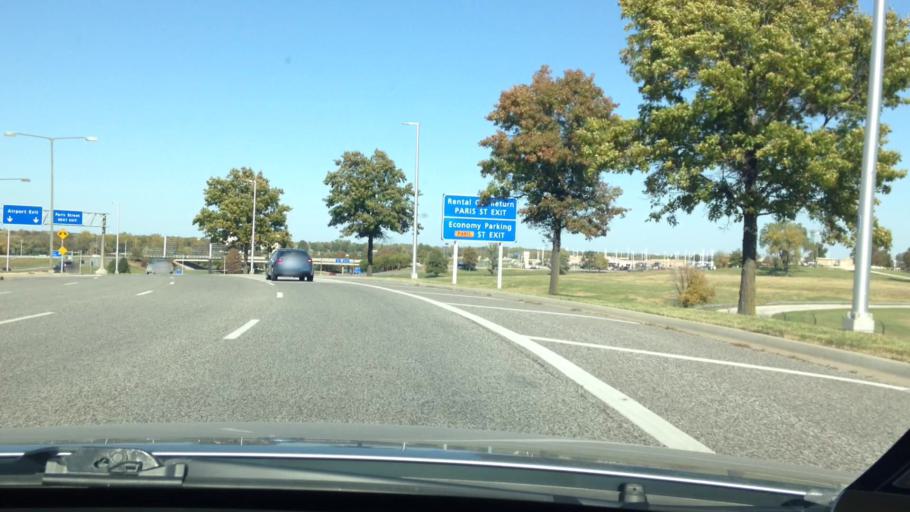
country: US
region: Missouri
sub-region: Platte County
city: Weatherby Lake
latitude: 39.2975
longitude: -94.7136
